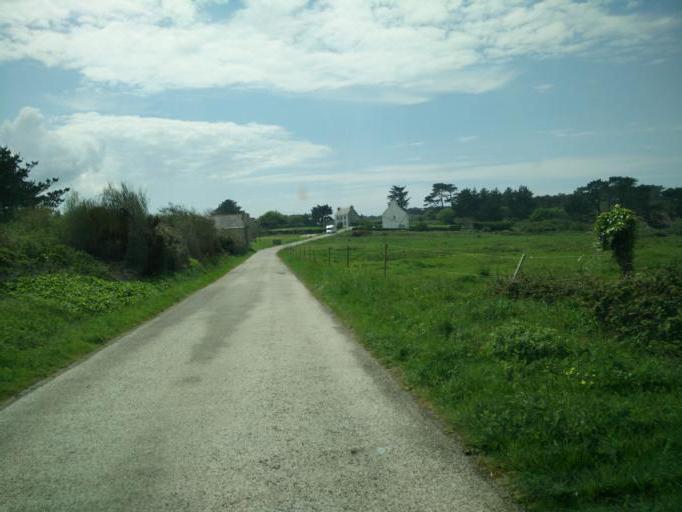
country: FR
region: Brittany
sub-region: Departement du Finistere
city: Roscanvel
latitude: 48.3264
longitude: -4.5695
